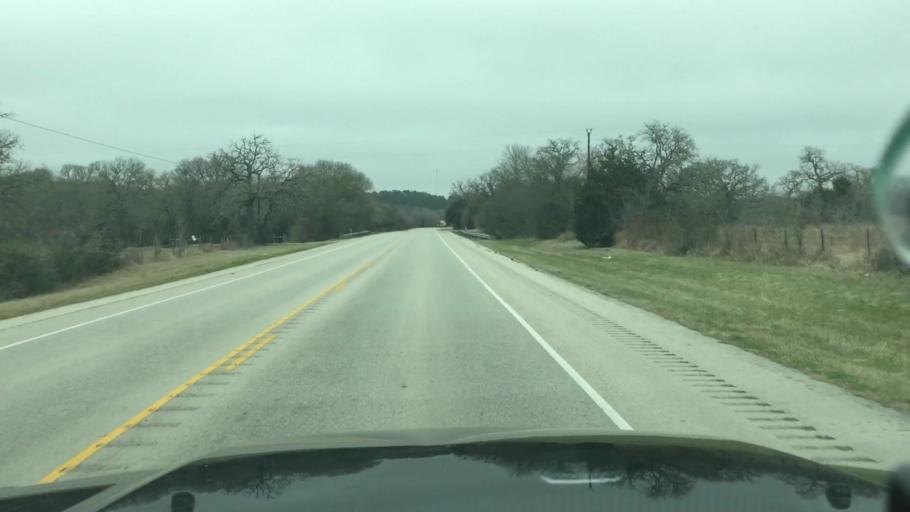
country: US
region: Texas
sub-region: Fayette County
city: La Grange
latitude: 30.0291
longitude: -96.9058
